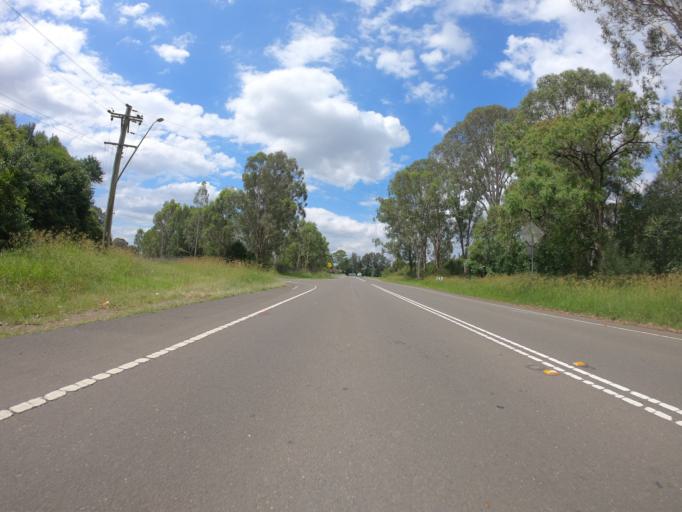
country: AU
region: New South Wales
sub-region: Blacktown
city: Mount Druitt
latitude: -33.8044
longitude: 150.7671
